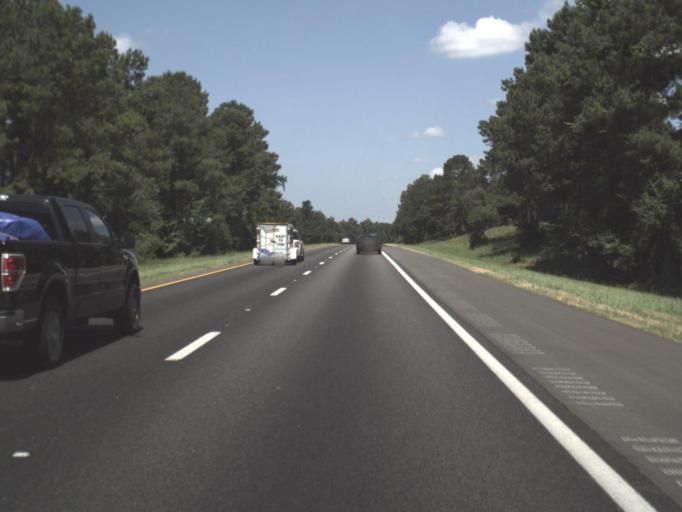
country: US
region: Florida
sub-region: Madison County
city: Madison
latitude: 30.4121
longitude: -83.4247
